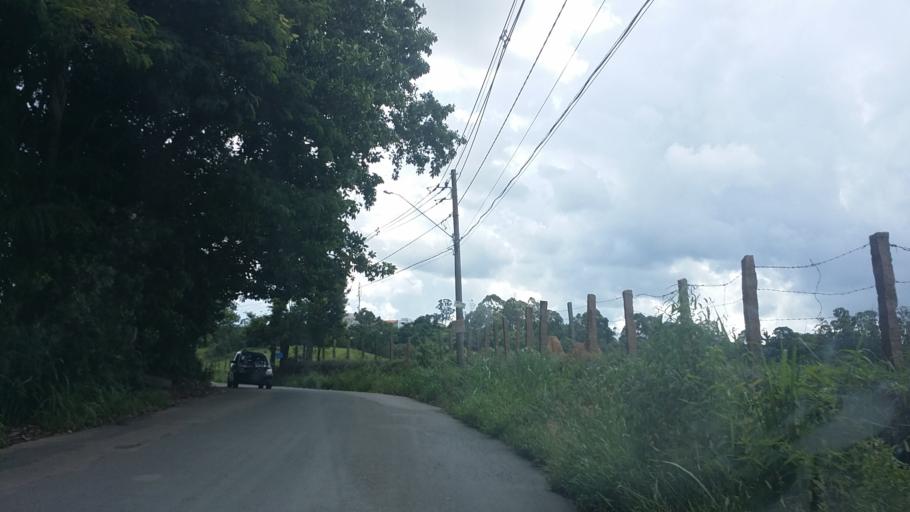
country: BR
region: Sao Paulo
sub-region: Itupeva
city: Itupeva
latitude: -23.1600
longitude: -47.0709
